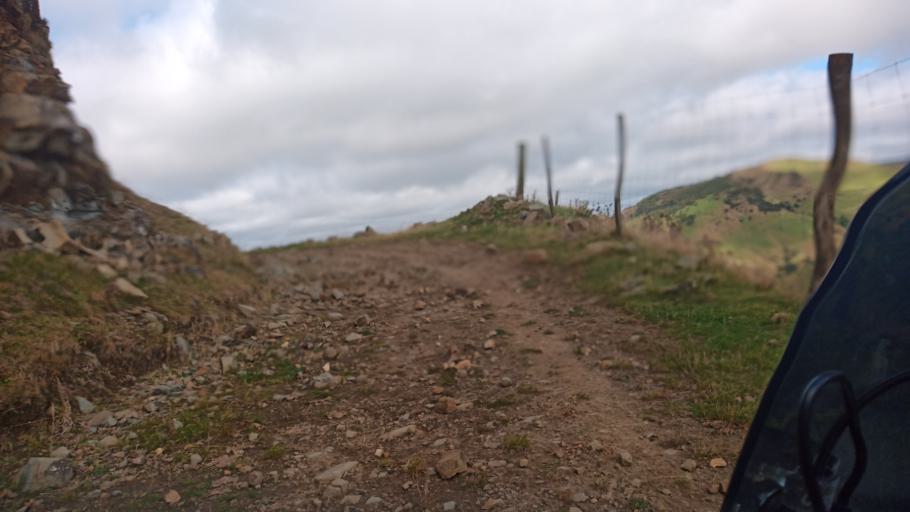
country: NZ
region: Gisborne
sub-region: Gisborne District
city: Gisborne
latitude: -38.4759
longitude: 177.5337
